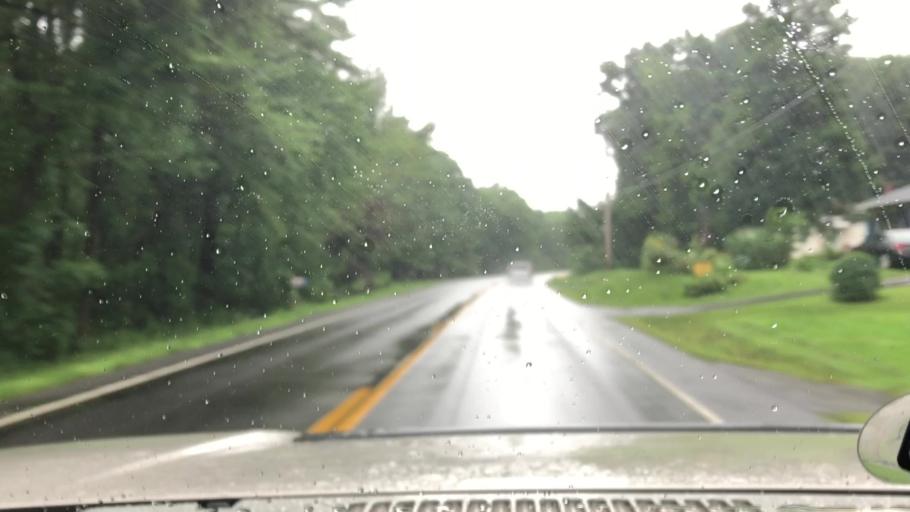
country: US
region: New York
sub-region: Greene County
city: Cairo
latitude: 42.2840
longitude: -73.9833
